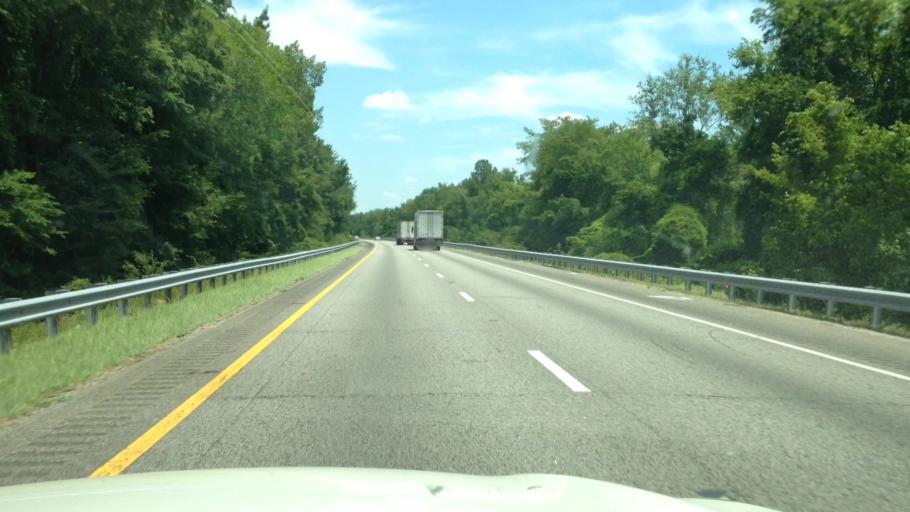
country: US
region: South Carolina
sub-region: Florence County
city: Florence
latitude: 34.2884
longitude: -79.6574
